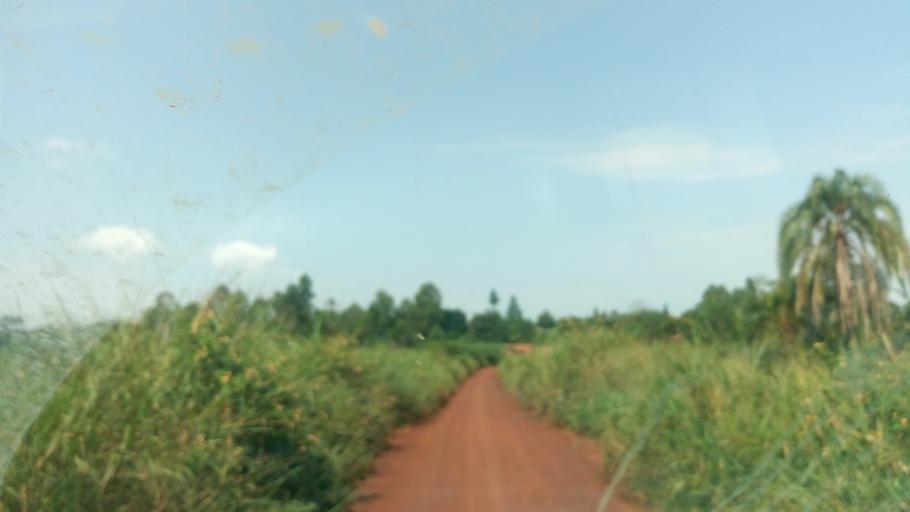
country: UG
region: Western Region
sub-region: Masindi District
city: Masindi
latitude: 1.6711
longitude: 31.8262
